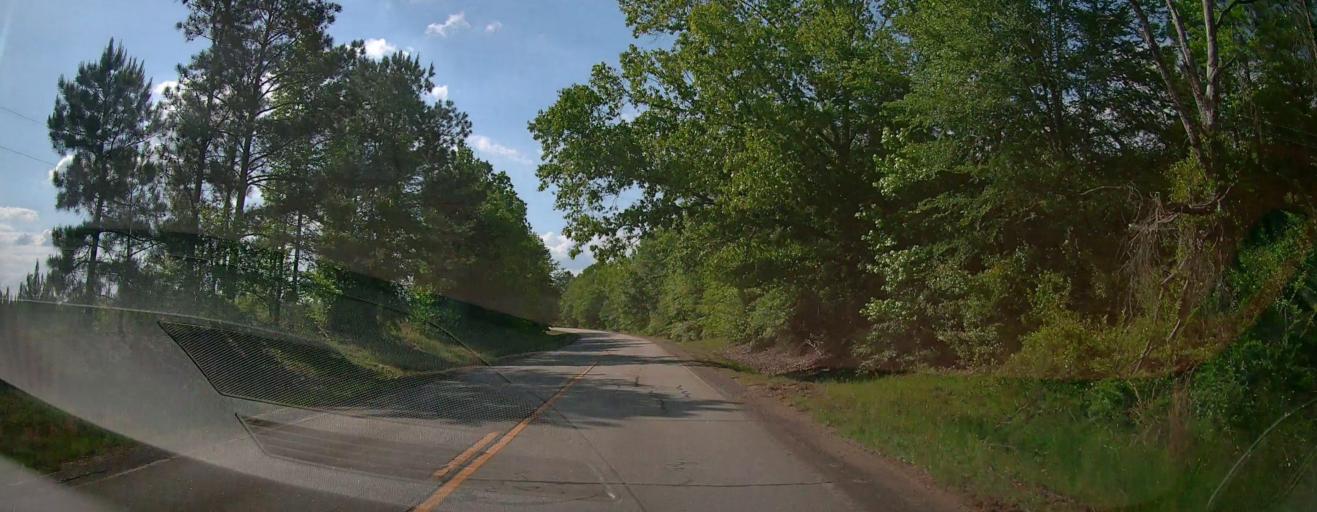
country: US
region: Georgia
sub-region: Washington County
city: Tennille
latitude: 32.9071
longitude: -82.9733
